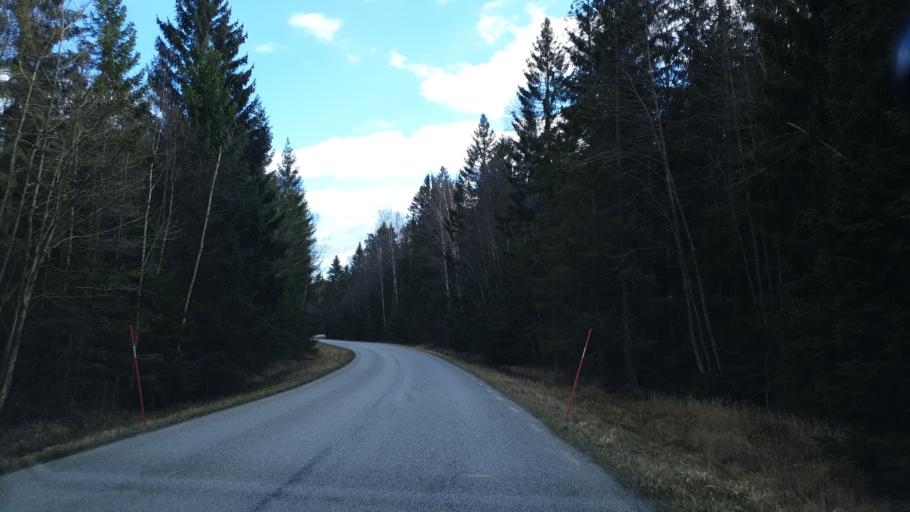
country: SE
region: Stockholm
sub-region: Varmdo Kommun
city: Hemmesta
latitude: 59.2388
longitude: 18.4769
